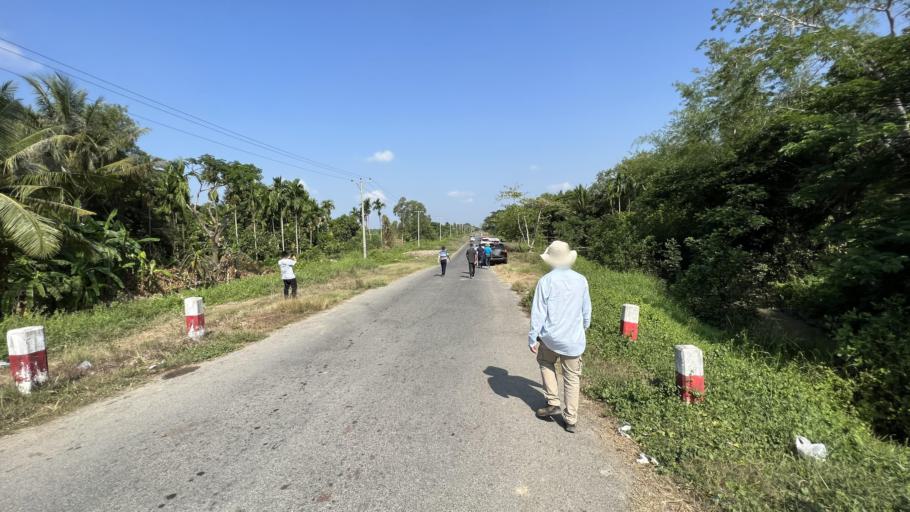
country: MM
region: Ayeyarwady
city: Kyaiklat
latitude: 16.4059
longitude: 95.8369
